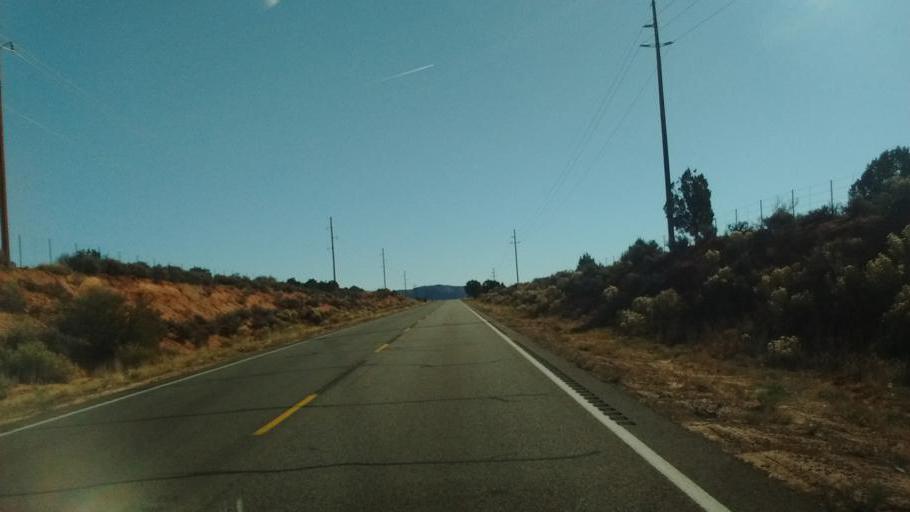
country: US
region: Arizona
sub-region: Mohave County
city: Colorado City
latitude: 37.0238
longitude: -113.0427
